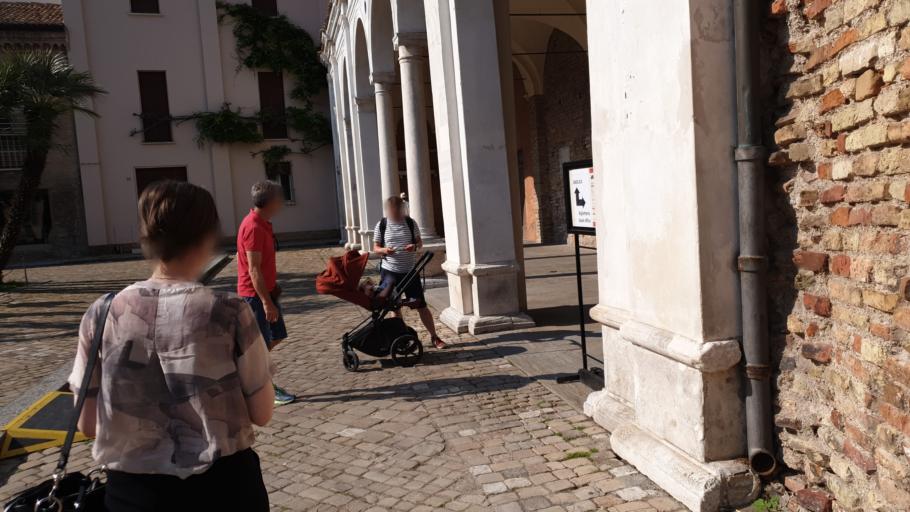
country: IT
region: Emilia-Romagna
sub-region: Provincia di Ravenna
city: Ravenna
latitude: 44.4166
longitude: 12.2046
